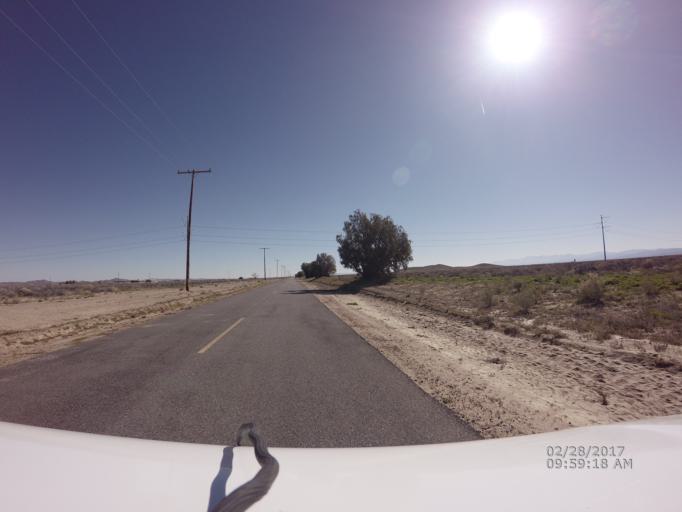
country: US
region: California
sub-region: Kern County
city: Rosamond
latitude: 34.8053
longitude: -118.3204
